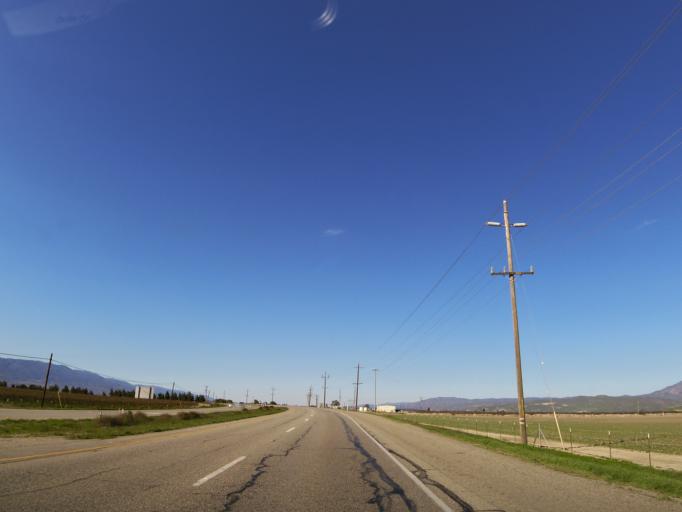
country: US
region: California
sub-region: Monterey County
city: Greenfield
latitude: 36.2912
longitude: -121.1978
